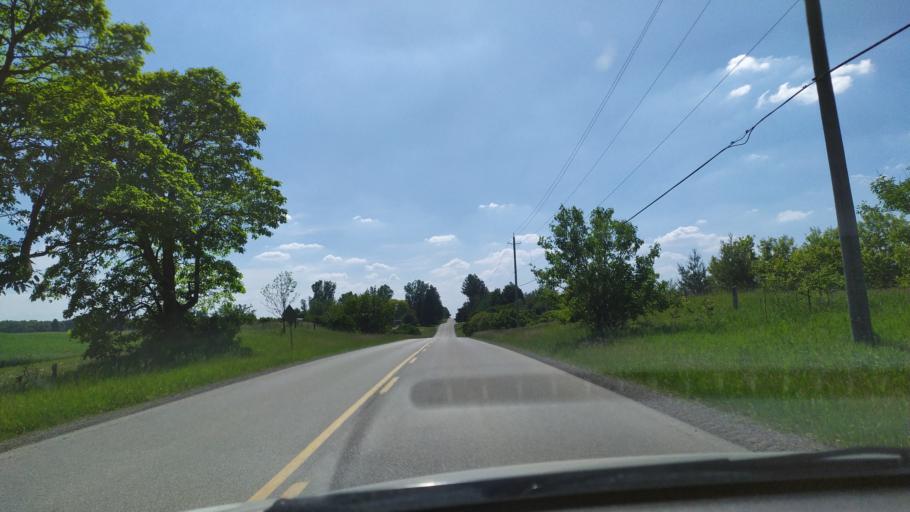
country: CA
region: Ontario
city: Kitchener
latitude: 43.3675
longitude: -80.5827
